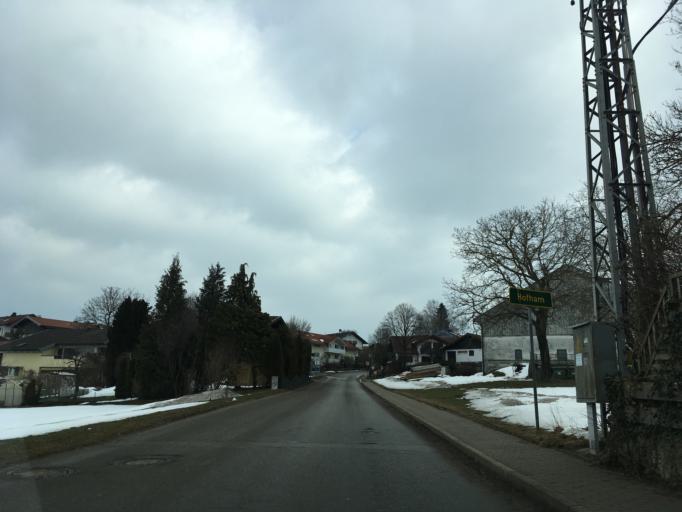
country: DE
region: Bavaria
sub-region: Upper Bavaria
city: Bad Endorf
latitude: 47.9044
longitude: 12.3117
